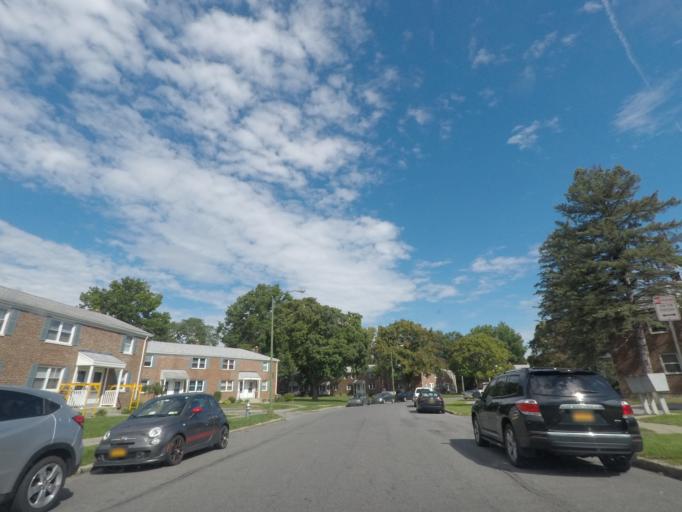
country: US
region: New York
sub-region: Albany County
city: Delmar
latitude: 42.6536
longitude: -73.8105
